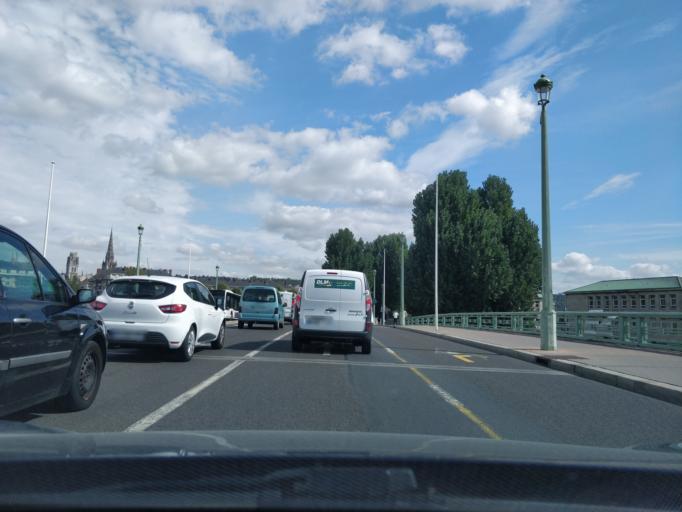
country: FR
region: Haute-Normandie
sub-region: Departement de la Seine-Maritime
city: Rouen
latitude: 49.4352
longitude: 1.0945
